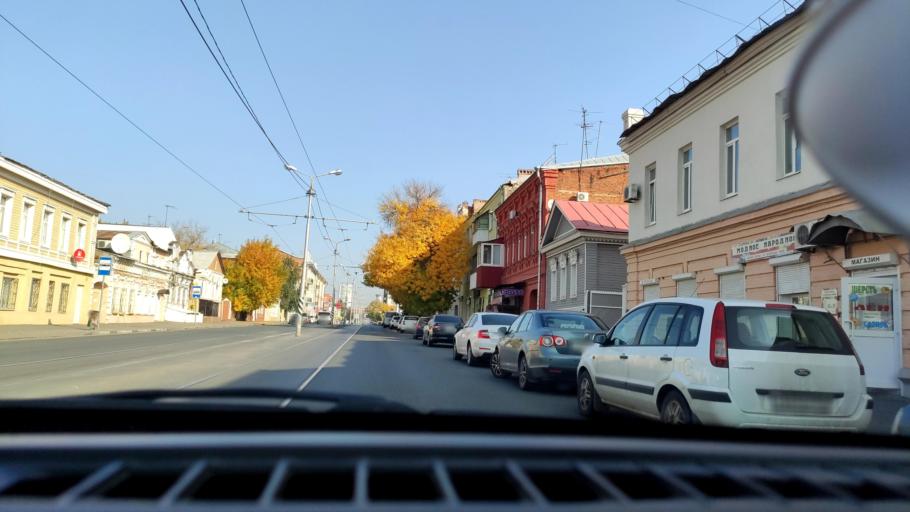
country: RU
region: Samara
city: Samara
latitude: 53.1883
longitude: 50.0998
